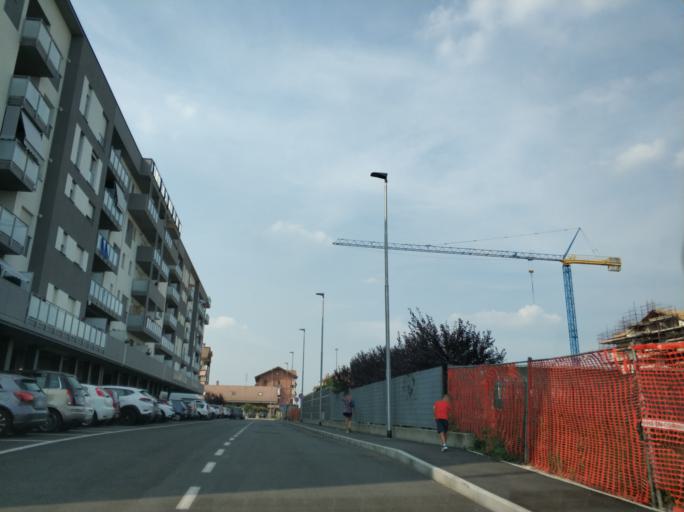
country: IT
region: Piedmont
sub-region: Provincia di Torino
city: Leini
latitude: 45.1511
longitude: 7.7043
